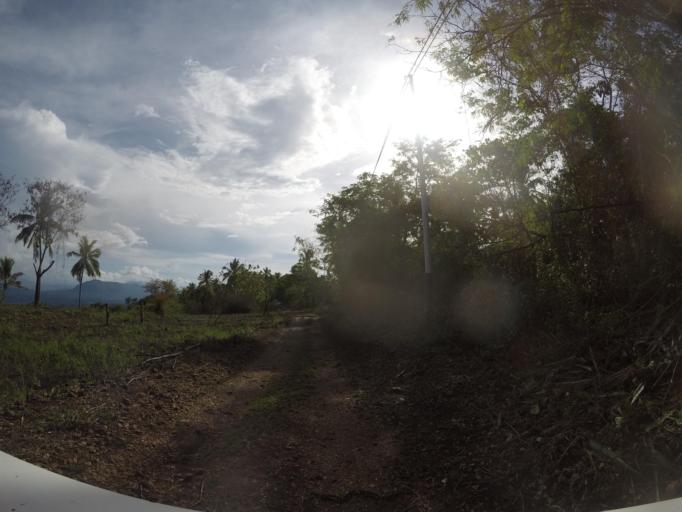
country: TL
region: Baucau
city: Baucau
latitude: -8.5023
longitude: 126.4520
